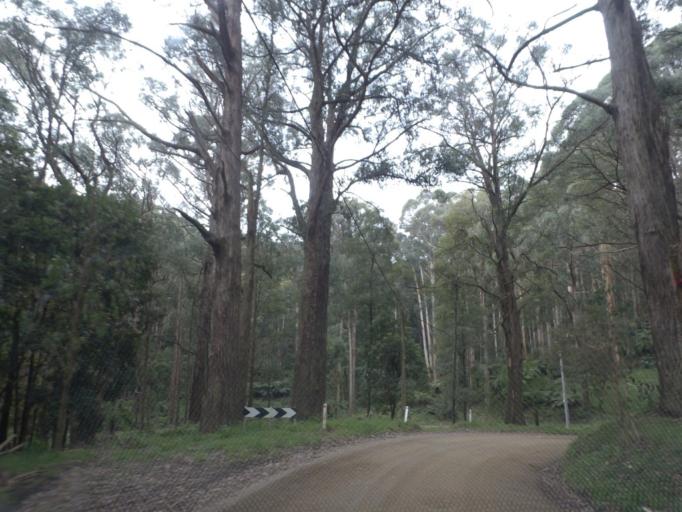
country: AU
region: Victoria
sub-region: Yarra Ranges
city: Olinda
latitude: -37.8578
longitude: 145.3448
